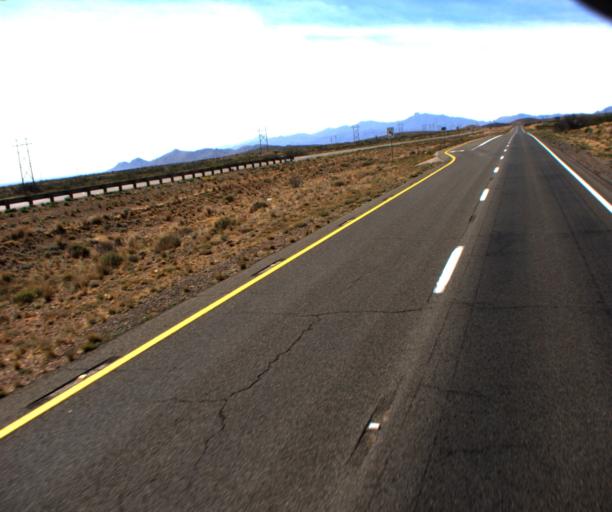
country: US
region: Arizona
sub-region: Graham County
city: Swift Trail Junction
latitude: 32.4971
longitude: -109.6739
